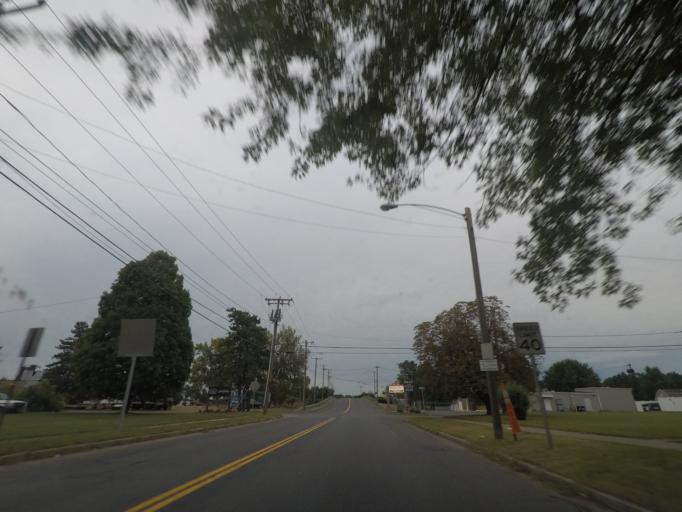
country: US
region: Massachusetts
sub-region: Hampden County
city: Ludlow
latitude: 42.1474
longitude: -72.5037
